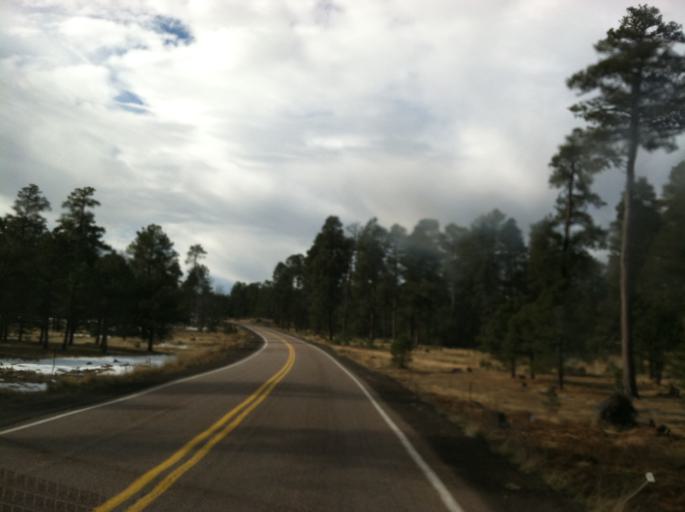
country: US
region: Arizona
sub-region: Navajo County
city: Heber-Overgaard
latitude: 34.3239
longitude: -110.8398
